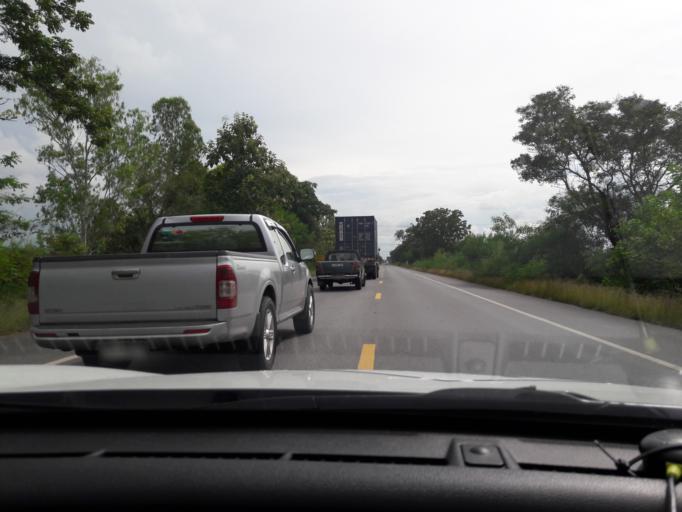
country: TH
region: Nakhon Sawan
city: Phai Sali
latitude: 15.5465
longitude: 100.5539
